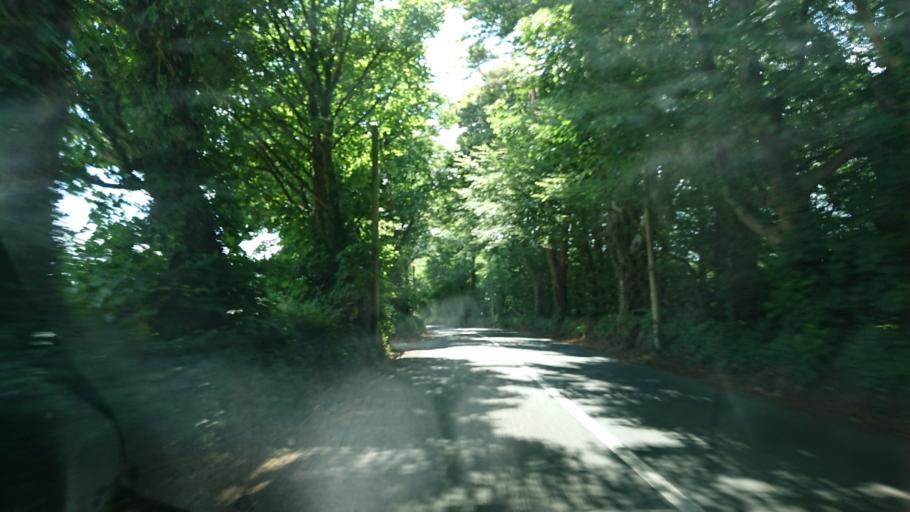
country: IE
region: Munster
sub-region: Waterford
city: Portlaw
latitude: 52.1688
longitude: -7.3362
